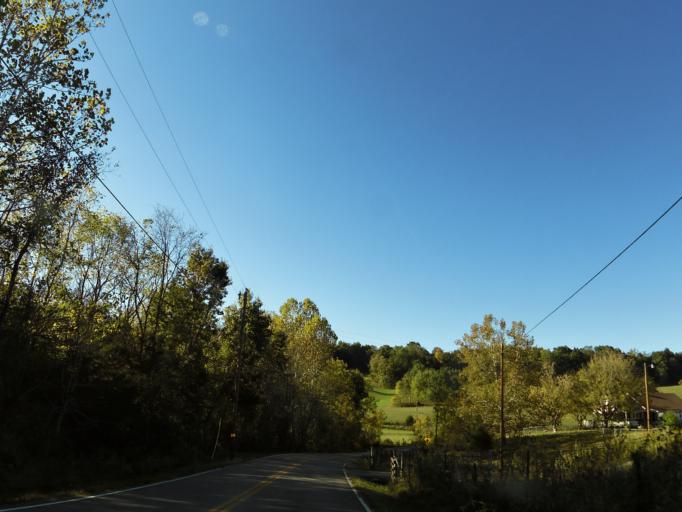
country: US
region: Tennessee
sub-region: Union County
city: Luttrell
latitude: 36.2592
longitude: -83.6543
